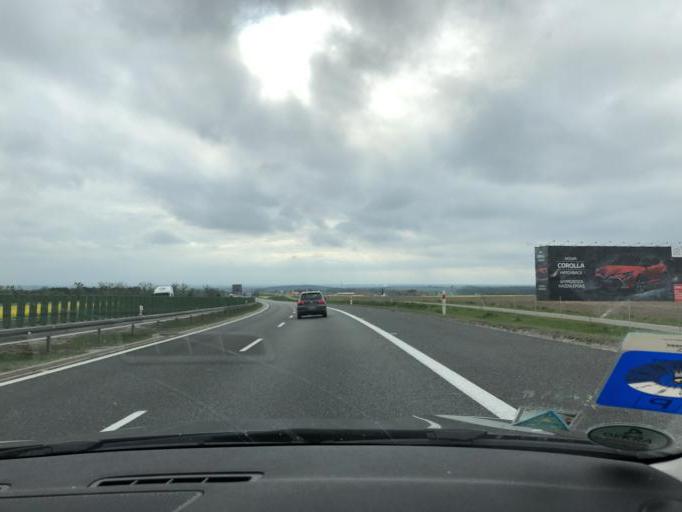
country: PL
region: Opole Voivodeship
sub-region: Powiat krapkowicki
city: Rozwadza
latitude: 50.4819
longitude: 18.1139
